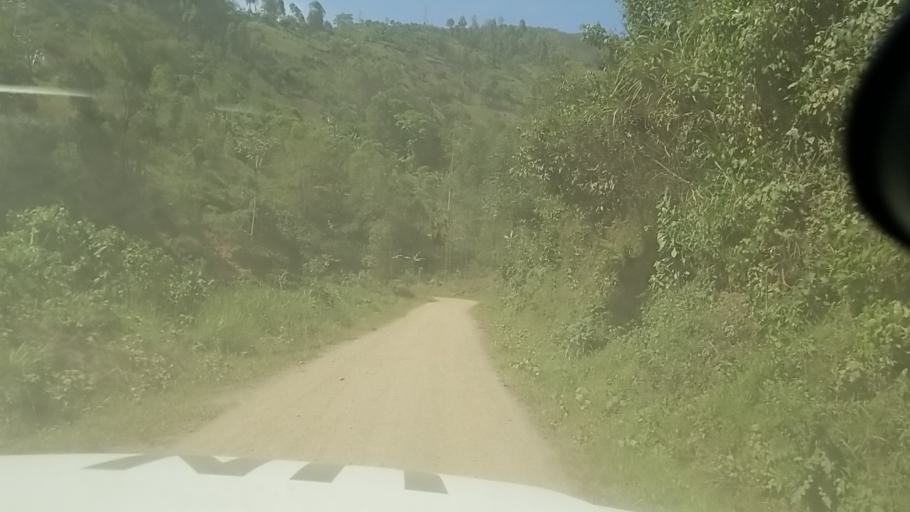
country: CD
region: Nord Kivu
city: Sake
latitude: -1.9404
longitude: 28.9279
